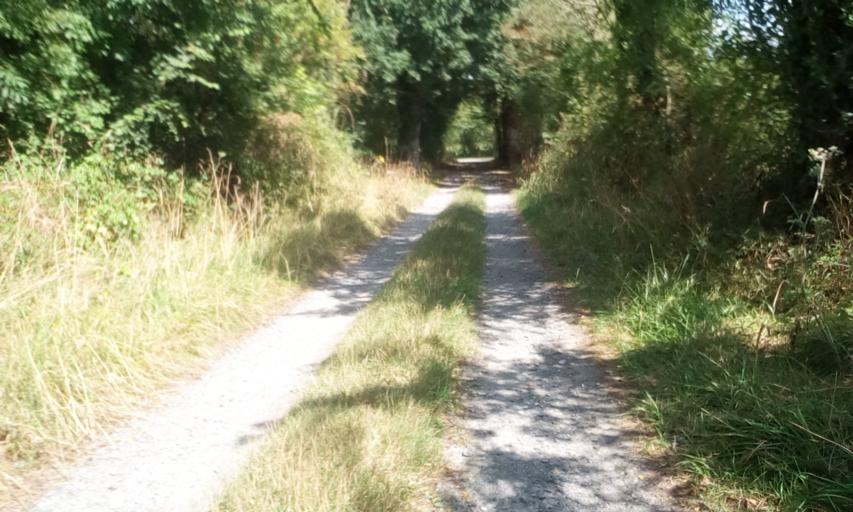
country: FR
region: Lower Normandy
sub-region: Departement du Calvados
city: Argences
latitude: 49.1329
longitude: -0.1557
